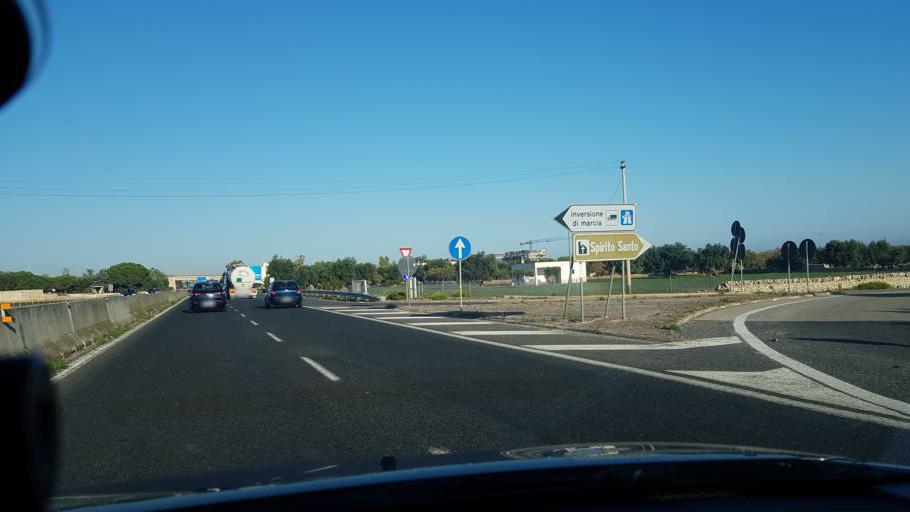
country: IT
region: Apulia
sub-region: Provincia di Bari
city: Monopoli
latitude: 40.9336
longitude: 17.2964
